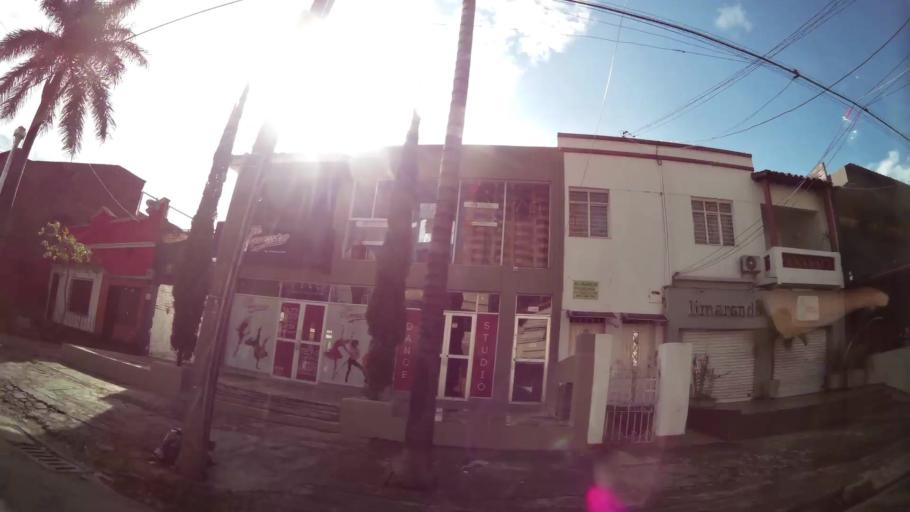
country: CO
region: Valle del Cauca
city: Cali
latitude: 3.4606
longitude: -76.5343
